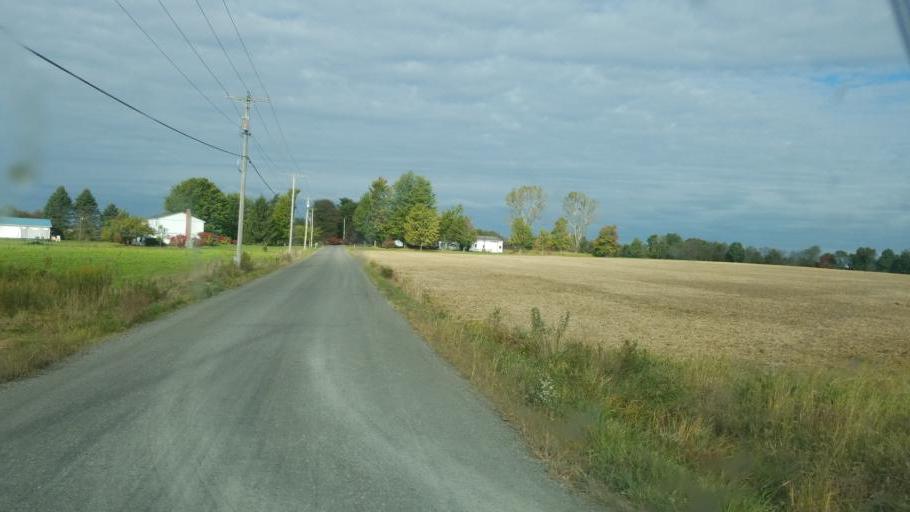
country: US
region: Pennsylvania
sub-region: Mercer County
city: Reynolds Heights
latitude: 41.3289
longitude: -80.2967
